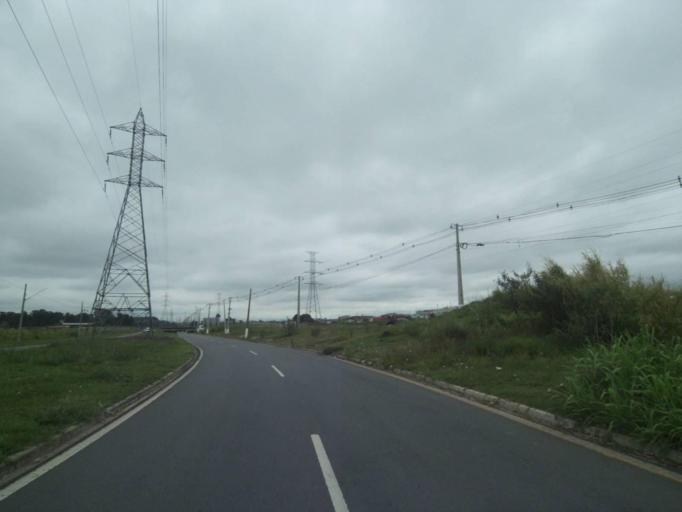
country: BR
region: Parana
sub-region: Araucaria
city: Araucaria
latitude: -25.5216
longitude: -49.3350
